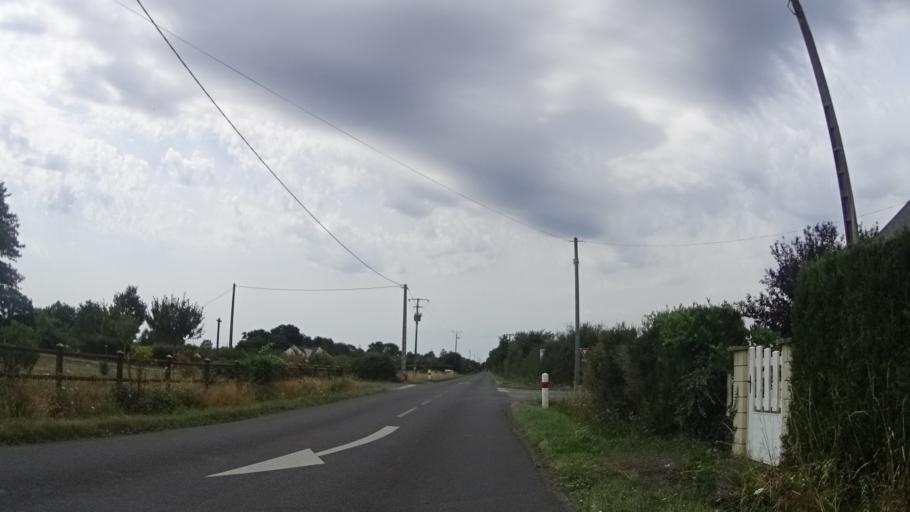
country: FR
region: Pays de la Loire
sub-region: Departement de la Loire-Atlantique
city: Heric
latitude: 47.4639
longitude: -1.6832
